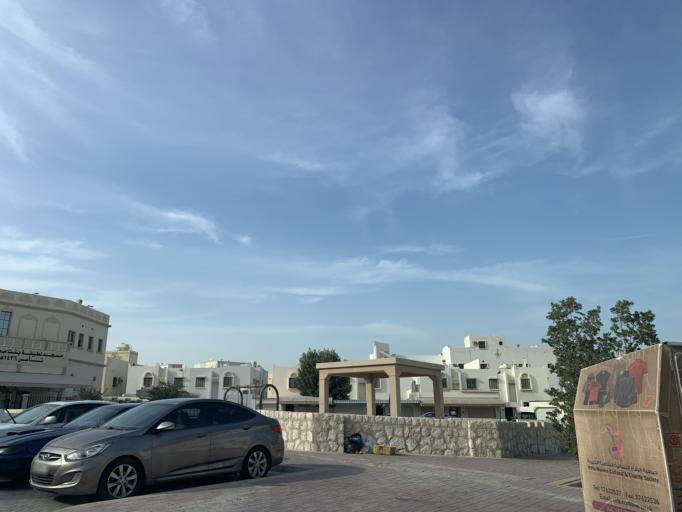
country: BH
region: Northern
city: Ar Rifa'
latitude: 26.1279
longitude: 50.5833
